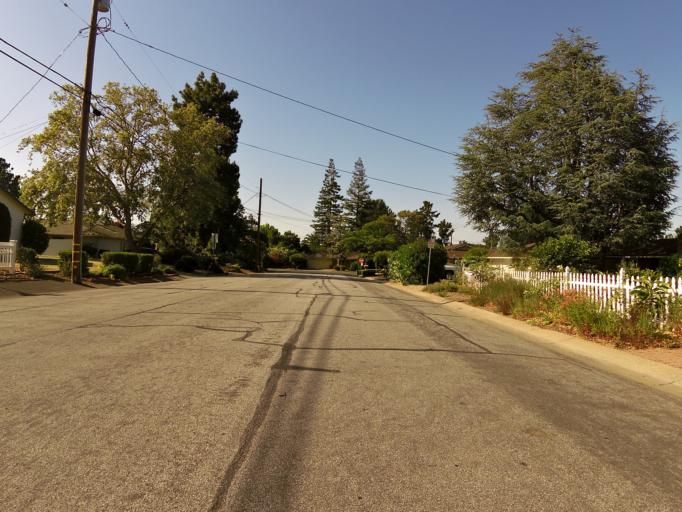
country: US
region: California
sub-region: Santa Clara County
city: Los Altos
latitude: 37.3878
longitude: -122.1067
